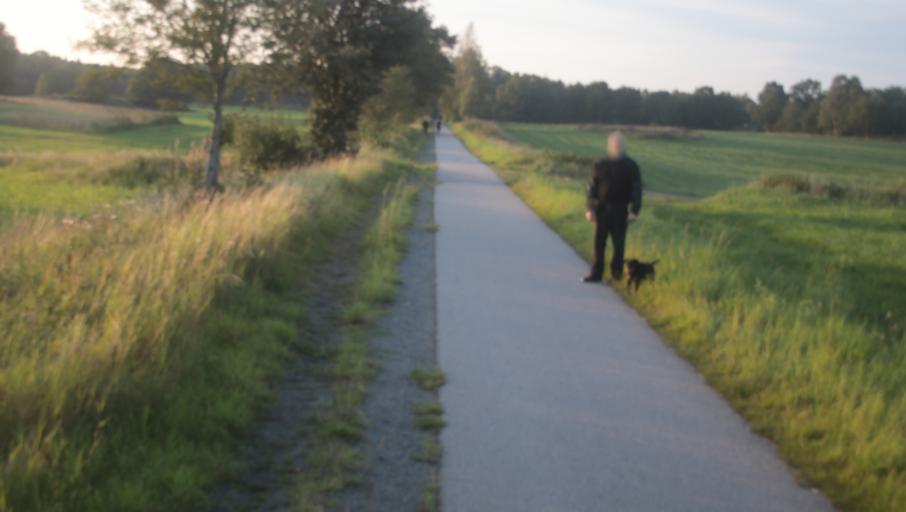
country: SE
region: Blekinge
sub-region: Karlshamns Kommun
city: Karlshamn
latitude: 56.2153
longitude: 14.8248
